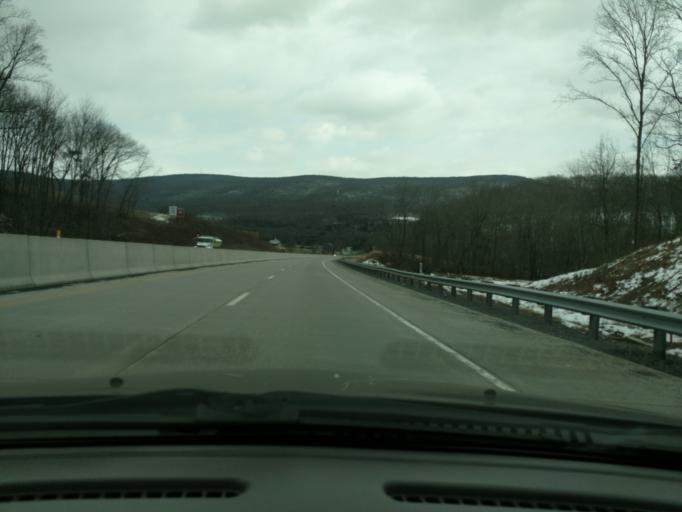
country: US
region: Pennsylvania
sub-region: Schuylkill County
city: Orwigsburg
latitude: 40.6142
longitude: -76.0384
